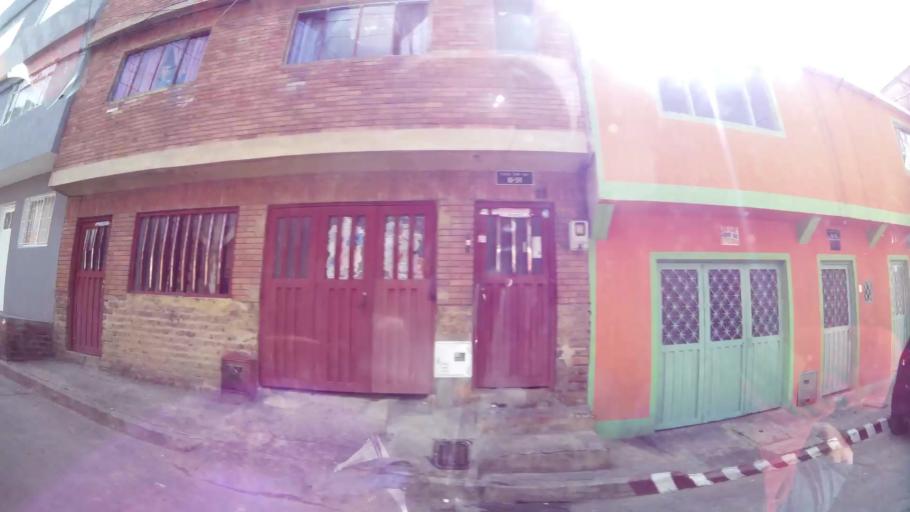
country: CO
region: Bogota D.C.
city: Bogota
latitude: 4.5635
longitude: -74.1046
